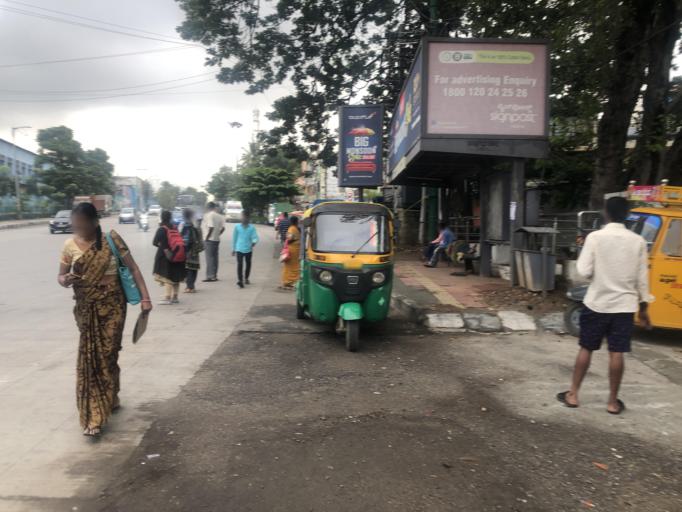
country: IN
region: Karnataka
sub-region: Bangalore Urban
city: Bangalore
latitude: 12.9509
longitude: 77.5389
